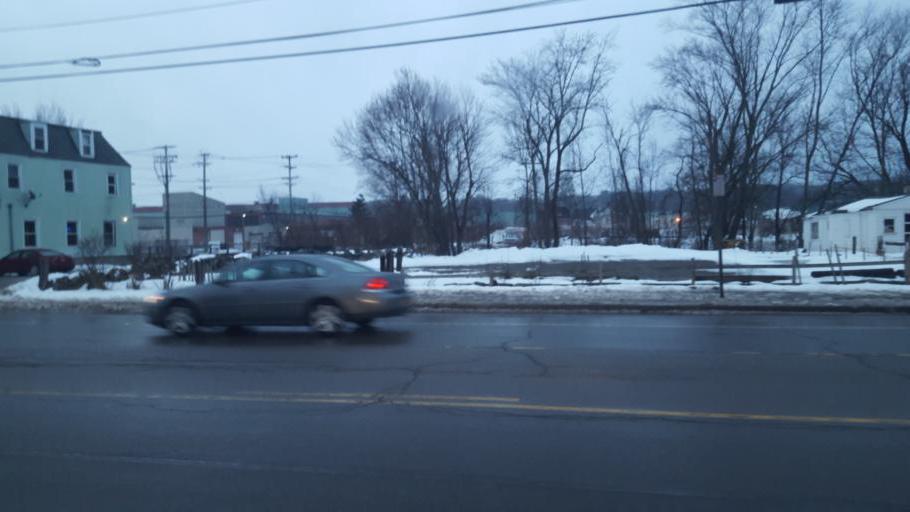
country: US
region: New York
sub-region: Chautauqua County
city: Falconer
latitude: 42.1136
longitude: -79.2080
